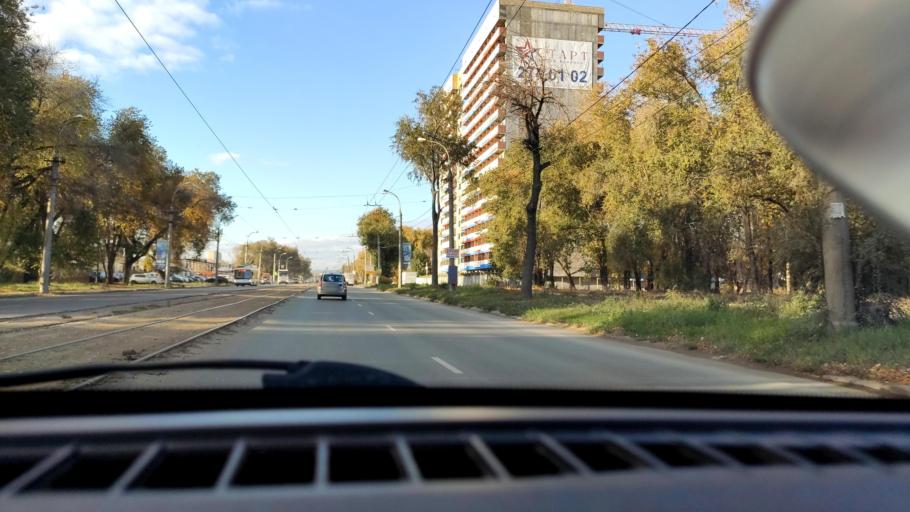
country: RU
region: Samara
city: Smyshlyayevka
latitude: 53.2007
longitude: 50.2848
